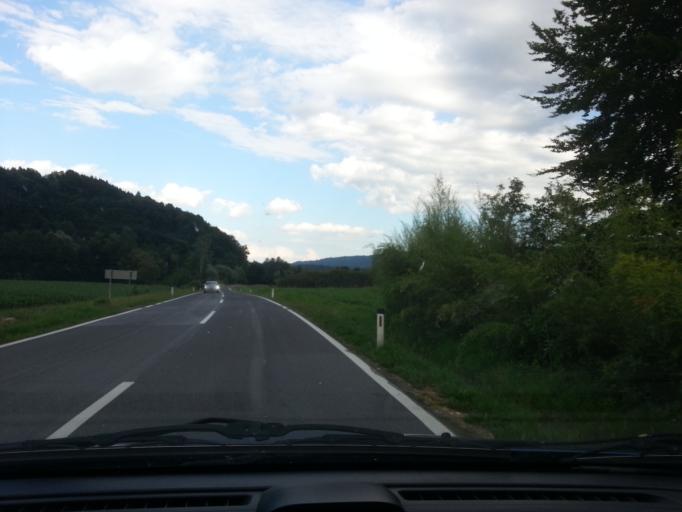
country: AT
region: Styria
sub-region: Politischer Bezirk Leibnitz
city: Oberhaag
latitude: 46.6923
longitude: 15.3221
